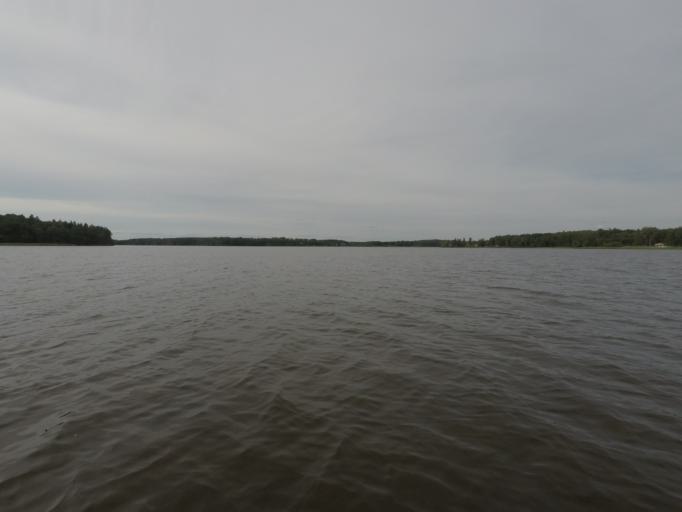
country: SE
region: Soedermanland
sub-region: Eskilstuna Kommun
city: Torshalla
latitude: 59.4815
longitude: 16.4158
